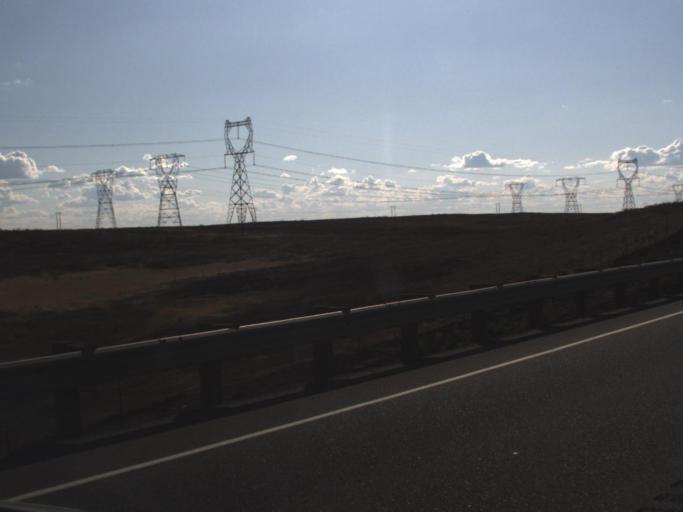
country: US
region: Oregon
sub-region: Morrow County
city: Irrigon
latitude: 45.9450
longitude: -119.5006
